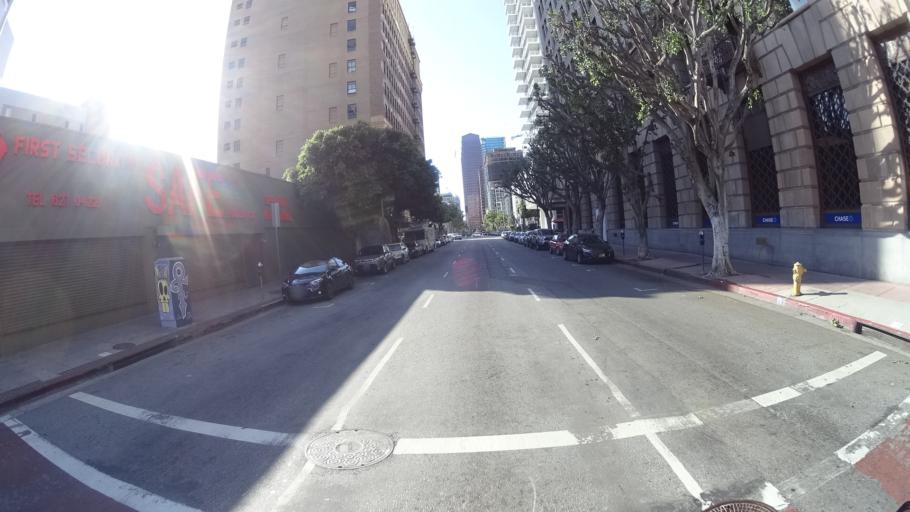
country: US
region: California
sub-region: Los Angeles County
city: Los Angeles
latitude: 34.0431
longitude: -118.2574
